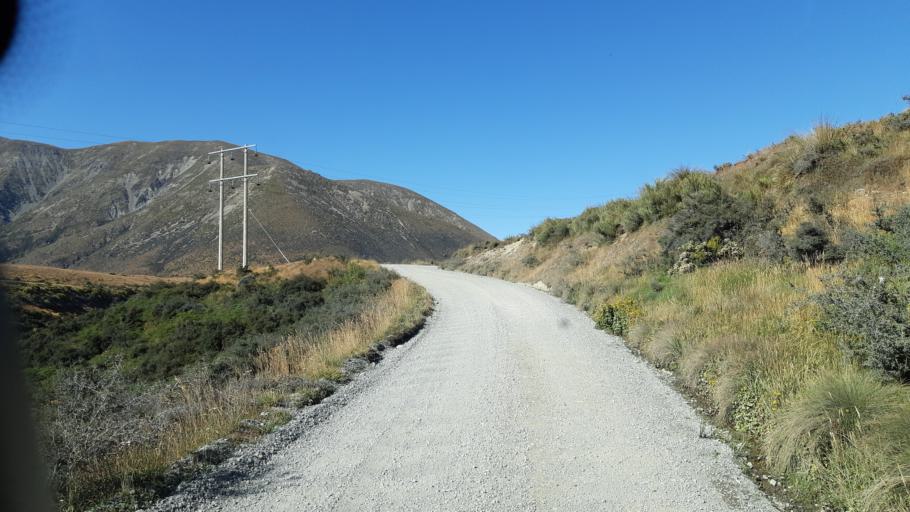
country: NZ
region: Canterbury
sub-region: Ashburton District
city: Methven
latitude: -43.3293
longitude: 171.6746
